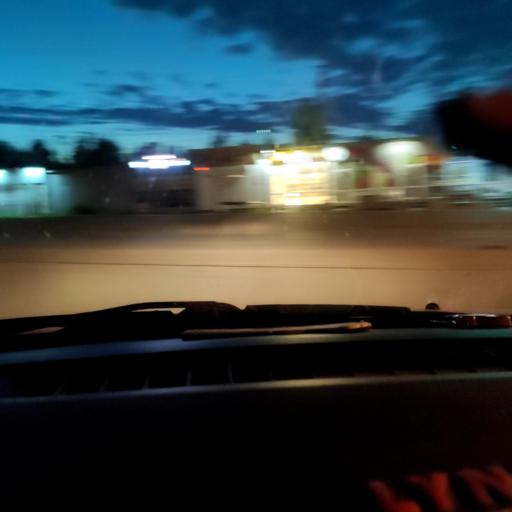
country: RU
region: Perm
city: Novyye Lyady
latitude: 58.0525
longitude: 56.5839
